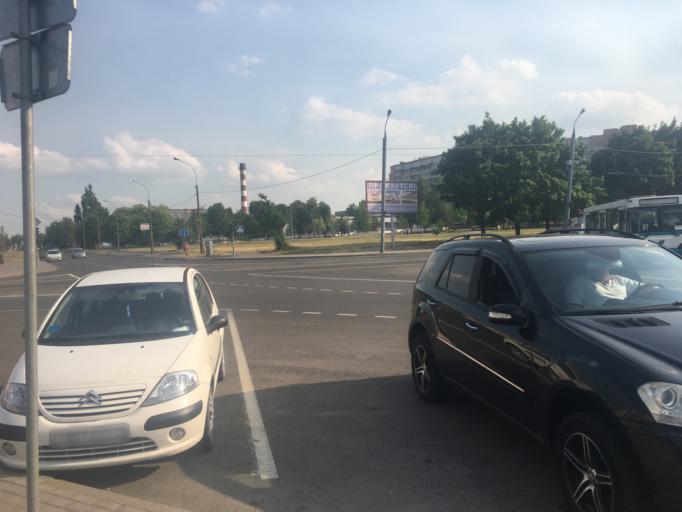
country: BY
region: Grodnenskaya
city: Hrodna
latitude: 53.6642
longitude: 23.8015
